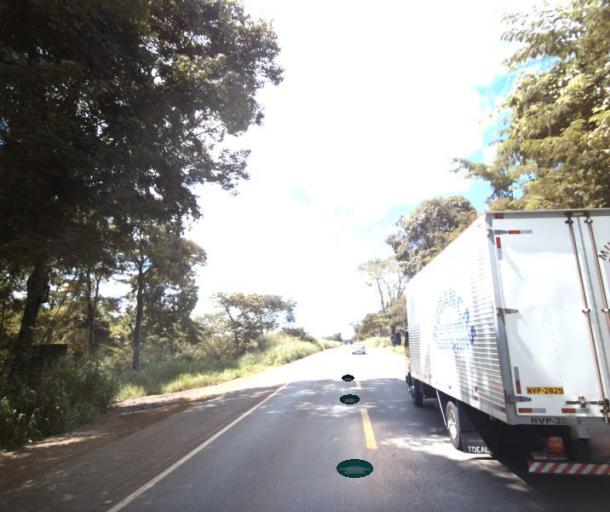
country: BR
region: Goias
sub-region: Petrolina De Goias
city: Petrolina de Goias
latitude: -15.9617
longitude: -49.1790
